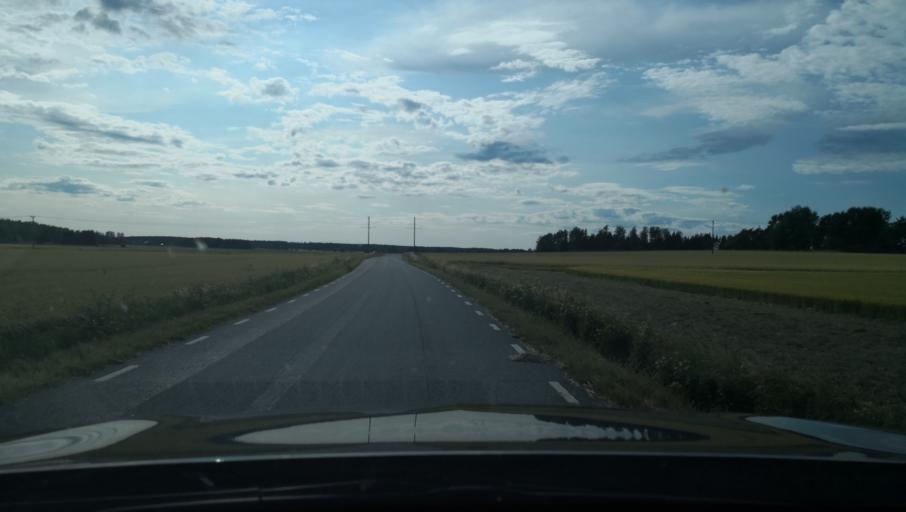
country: SE
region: Uppsala
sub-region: Enkopings Kommun
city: Orsundsbro
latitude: 59.7010
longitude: 17.2924
